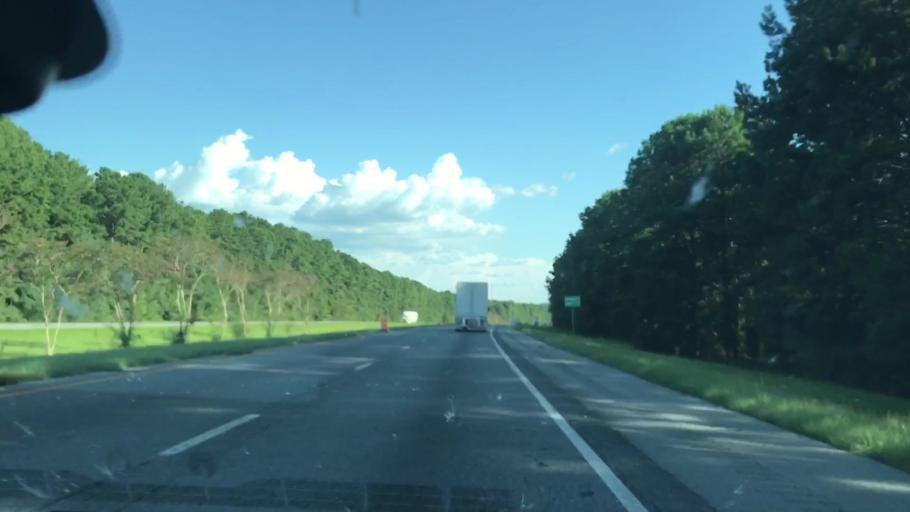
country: US
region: Georgia
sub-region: Harris County
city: Hamilton
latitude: 32.6546
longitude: -84.9748
